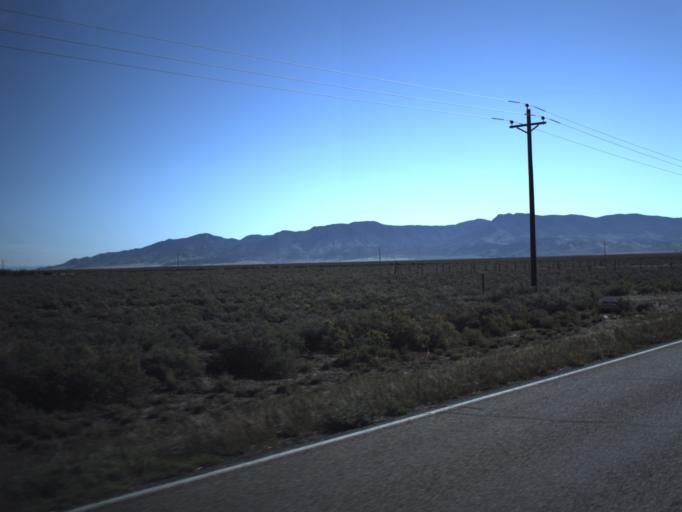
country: US
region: Utah
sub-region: Washington County
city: Enterprise
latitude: 37.6999
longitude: -113.6295
